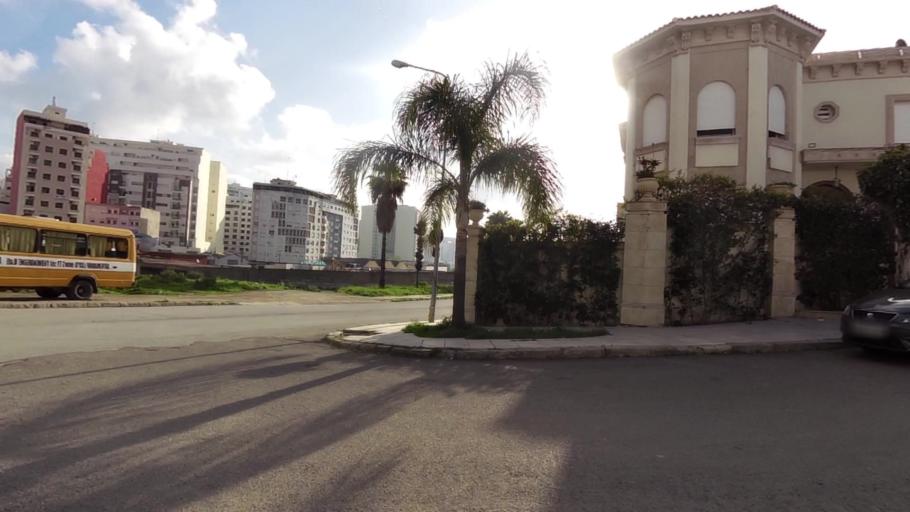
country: MA
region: Tanger-Tetouan
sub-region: Tanger-Assilah
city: Tangier
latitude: 35.7710
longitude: -5.7973
